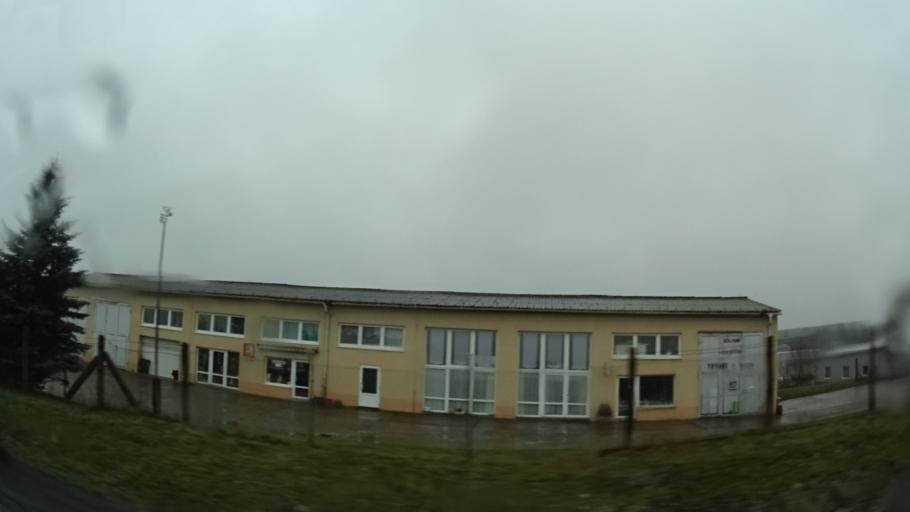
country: DE
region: Thuringia
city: Eisfeld
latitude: 50.4418
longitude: 10.9105
